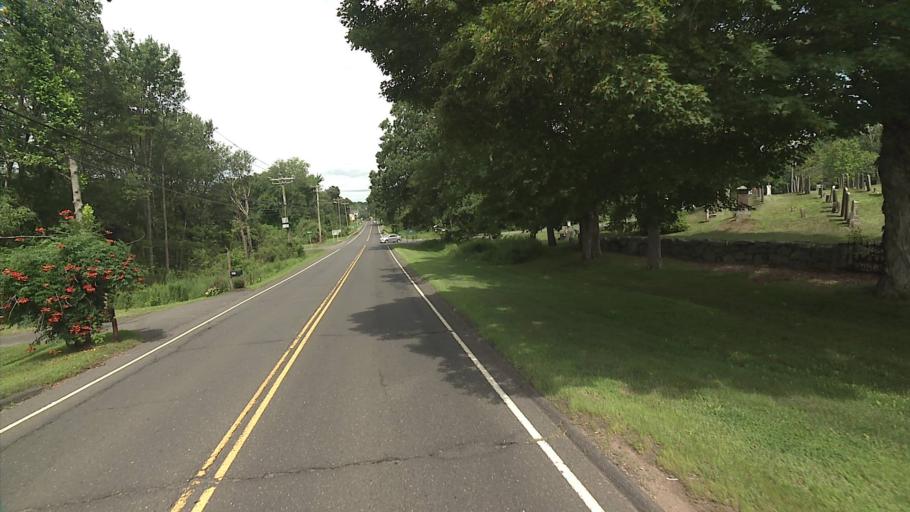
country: US
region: Connecticut
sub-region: New Haven County
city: Oxford
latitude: 41.4610
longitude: -73.1569
